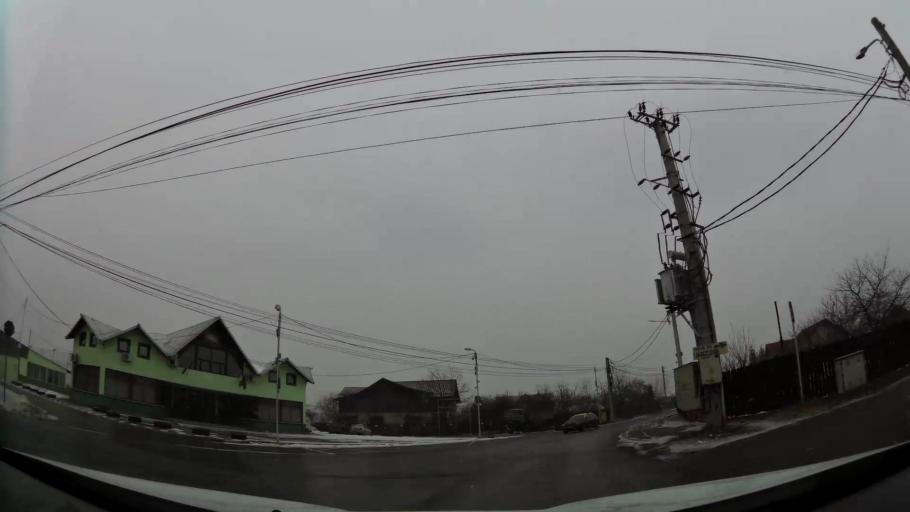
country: RO
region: Prahova
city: Ploiesti
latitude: 44.9567
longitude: 26.0392
